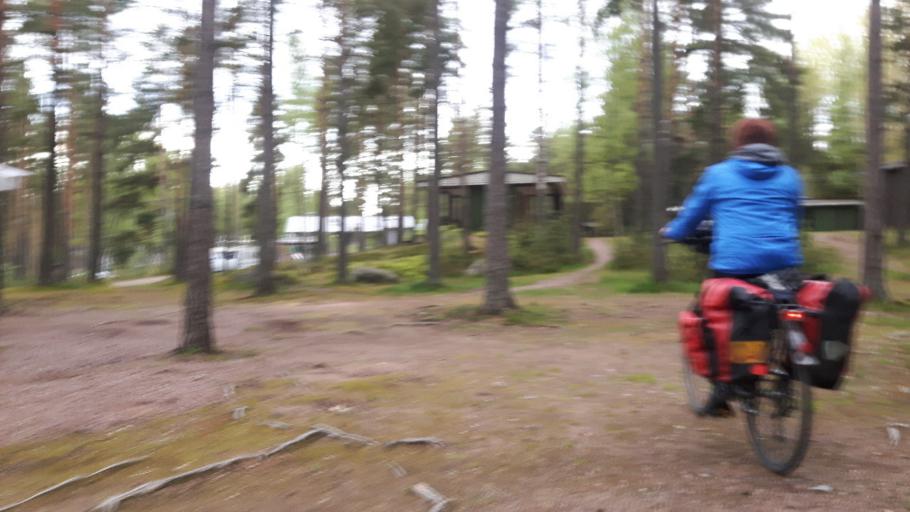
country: FI
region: Kymenlaakso
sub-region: Kotka-Hamina
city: Hamina
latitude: 60.5260
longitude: 27.2542
